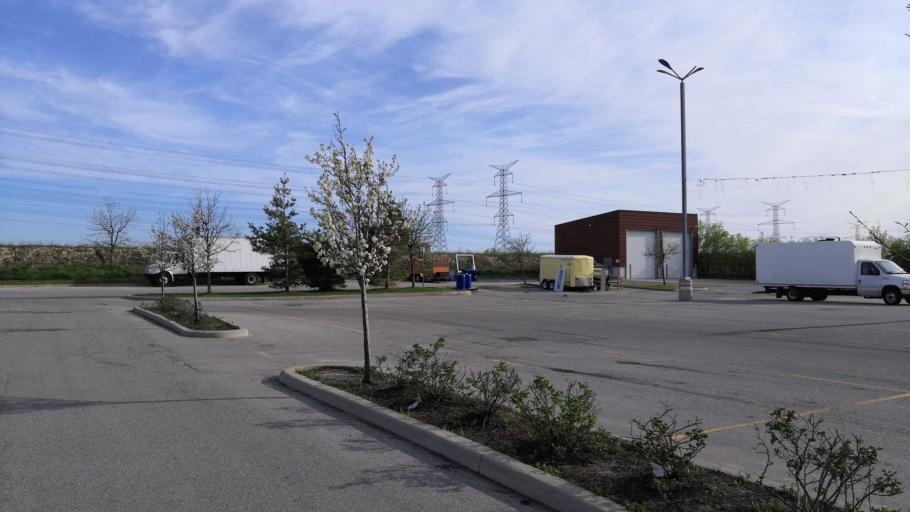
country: CA
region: Ontario
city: Concord
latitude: 43.7861
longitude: -79.4984
